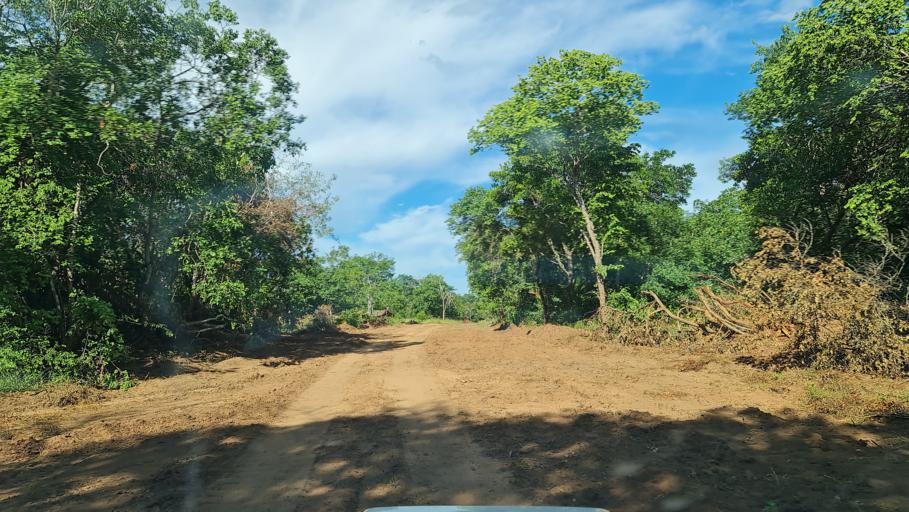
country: MZ
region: Nampula
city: Antonio Enes
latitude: -15.5090
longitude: 40.1372
